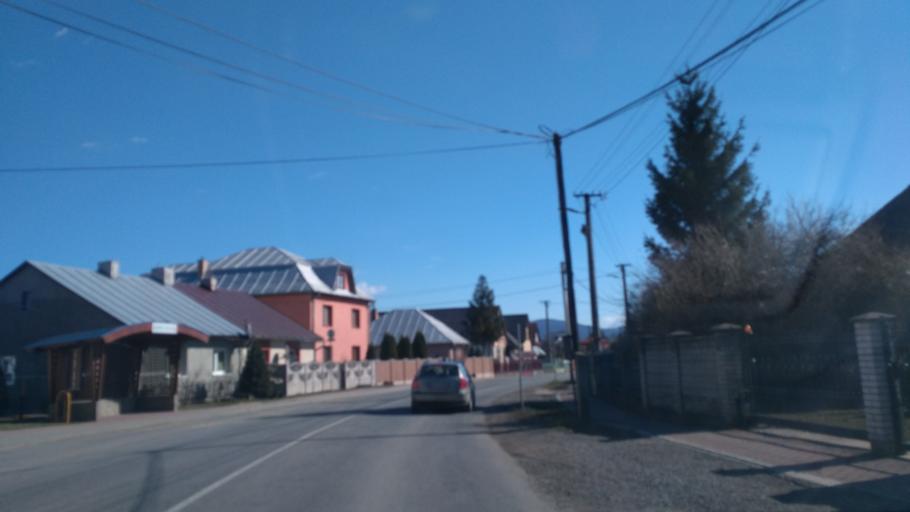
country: SK
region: Kosicky
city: Kosice
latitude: 48.6307
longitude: 21.3039
